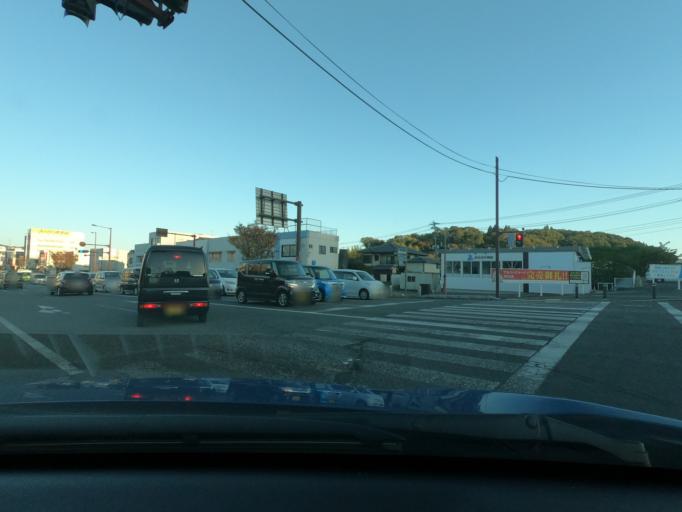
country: JP
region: Kagoshima
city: Satsumasendai
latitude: 31.8125
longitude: 130.3078
